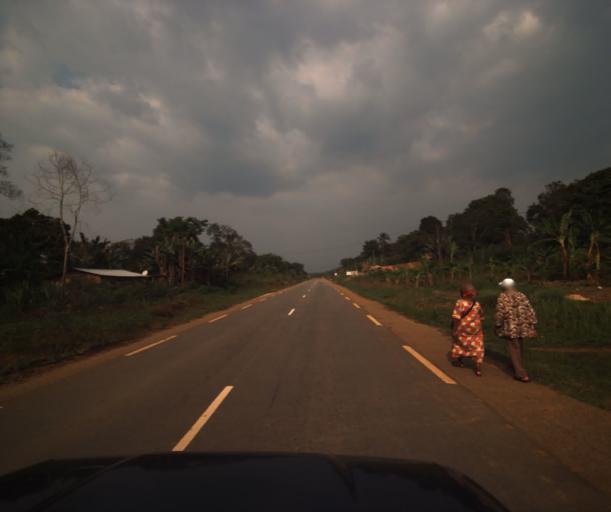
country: CM
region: Centre
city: Mbankomo
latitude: 3.7244
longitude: 11.3858
